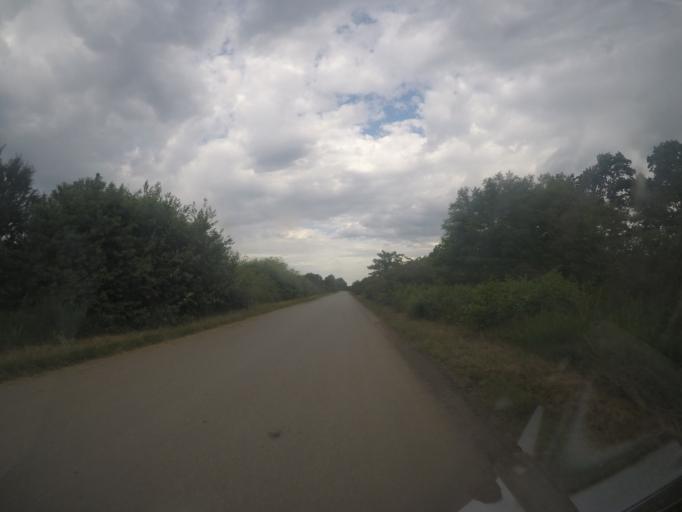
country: RS
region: Central Serbia
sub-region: Belgrade
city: Zemun
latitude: 44.8987
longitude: 20.4061
